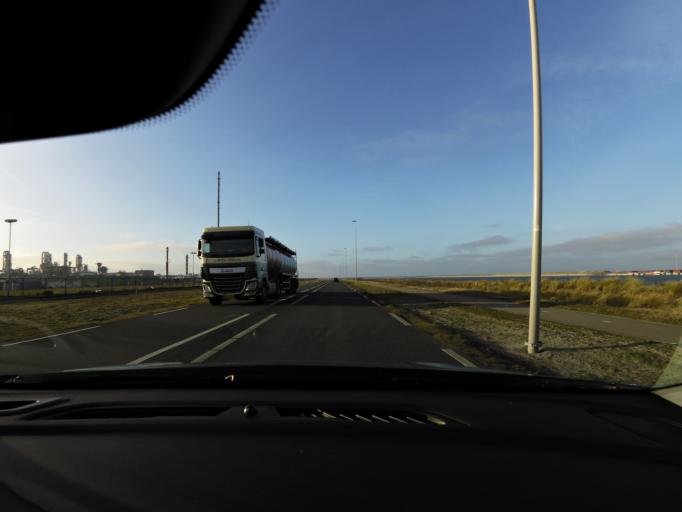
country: NL
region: South Holland
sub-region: Gemeente Rotterdam
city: Hoek van Holland
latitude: 51.9705
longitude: 4.0267
